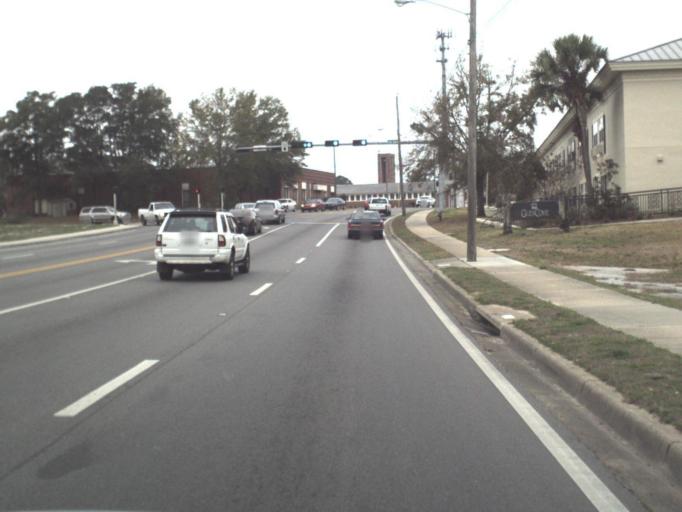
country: US
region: Florida
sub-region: Bay County
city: Panama City
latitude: 30.1564
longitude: -85.6450
